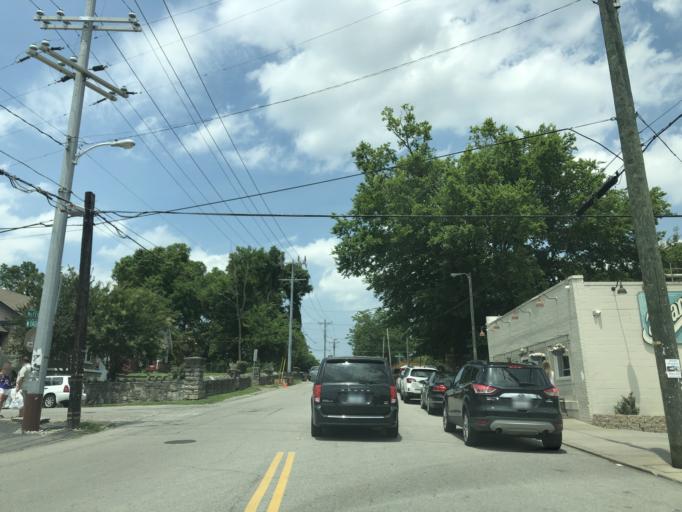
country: US
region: Tennessee
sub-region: Davidson County
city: Nashville
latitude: 36.1847
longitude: -86.7544
